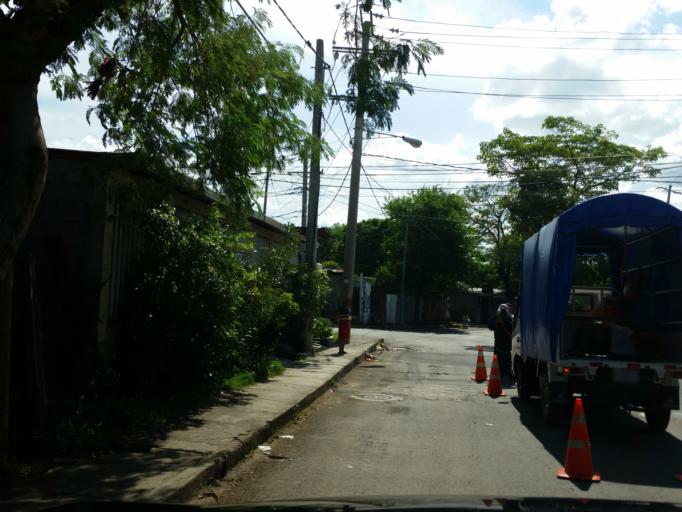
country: NI
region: Managua
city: Managua
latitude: 12.1558
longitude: -86.2267
